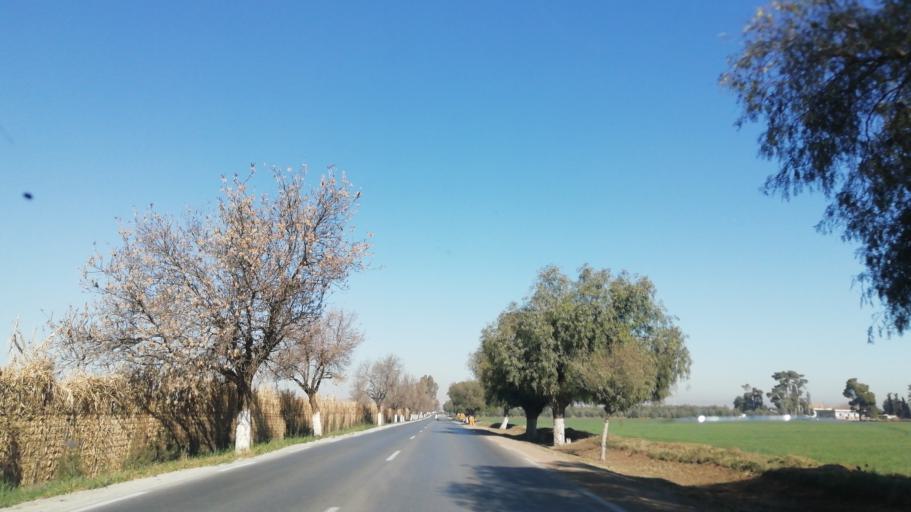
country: DZ
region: Mascara
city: Mascara
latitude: 35.2824
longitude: 0.1281
